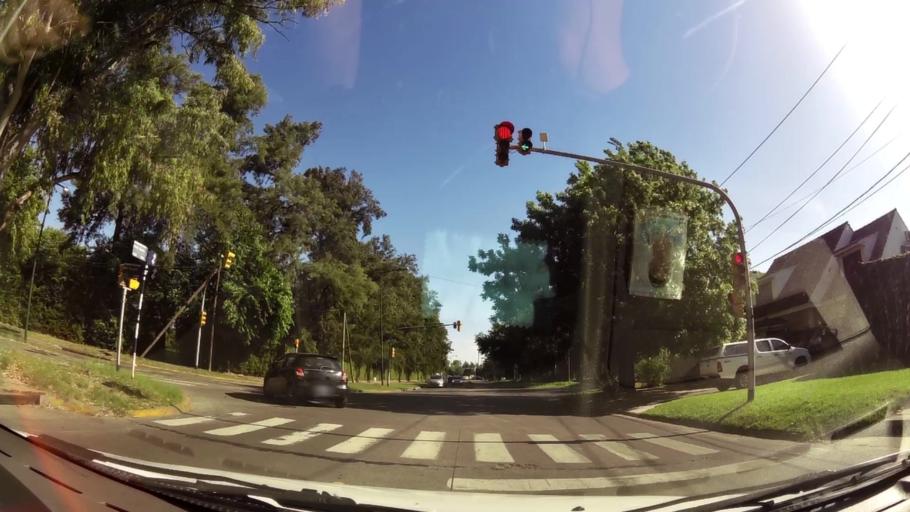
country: AR
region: Buenos Aires
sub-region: Partido de San Isidro
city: San Isidro
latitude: -34.4883
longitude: -58.5568
